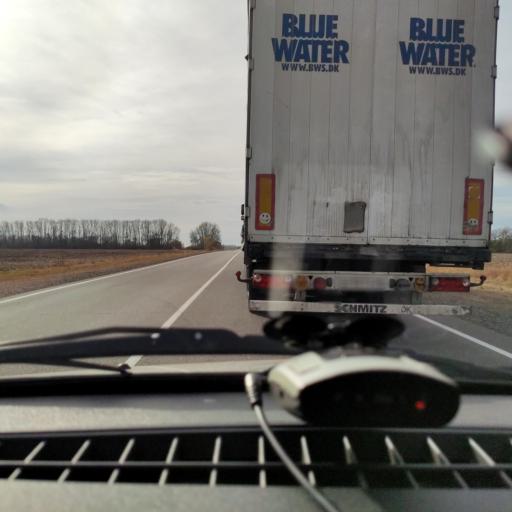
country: RU
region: Voronezj
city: Strelitsa
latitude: 51.5156
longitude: 38.9672
